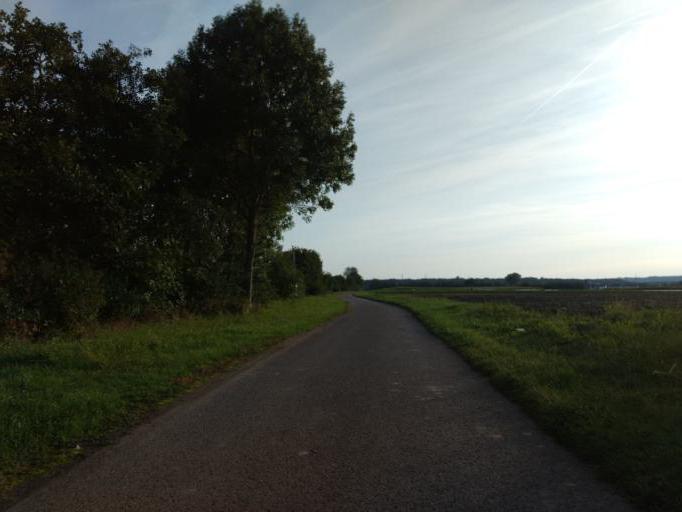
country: DE
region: Saarland
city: Ensdorf
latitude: 49.3150
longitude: 6.7722
